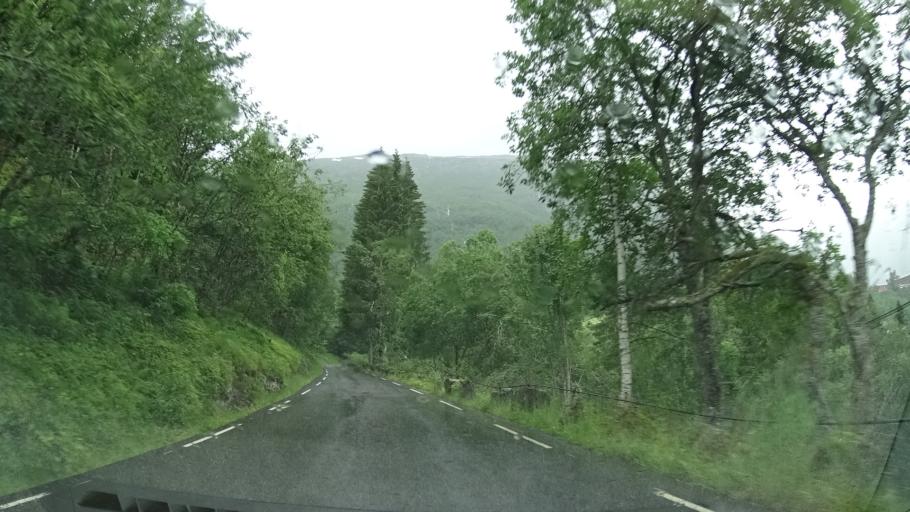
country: NO
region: Sogn og Fjordane
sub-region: Vik
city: Vik
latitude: 60.8306
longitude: 6.6801
